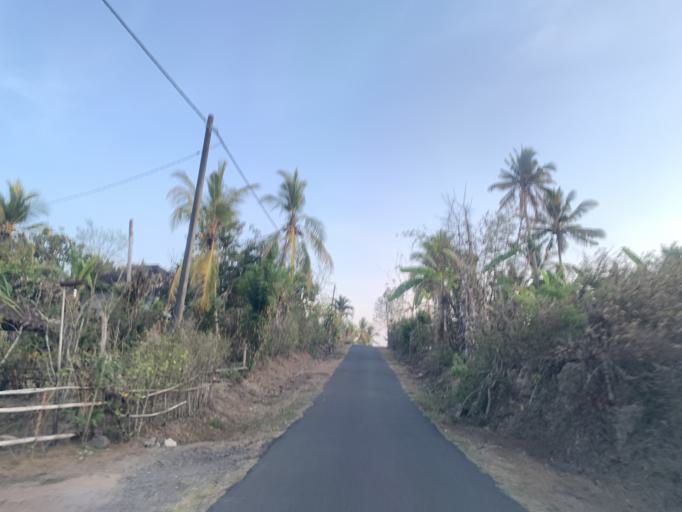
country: ID
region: Bali
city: Banjar Swastika
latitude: -8.4340
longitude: 114.8527
